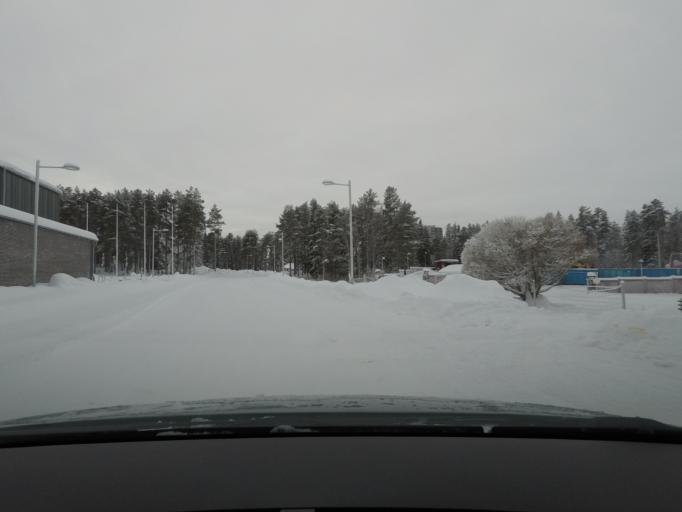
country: SE
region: Norrbotten
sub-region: Lulea Kommun
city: Lulea
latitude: 65.5950
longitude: 22.1917
